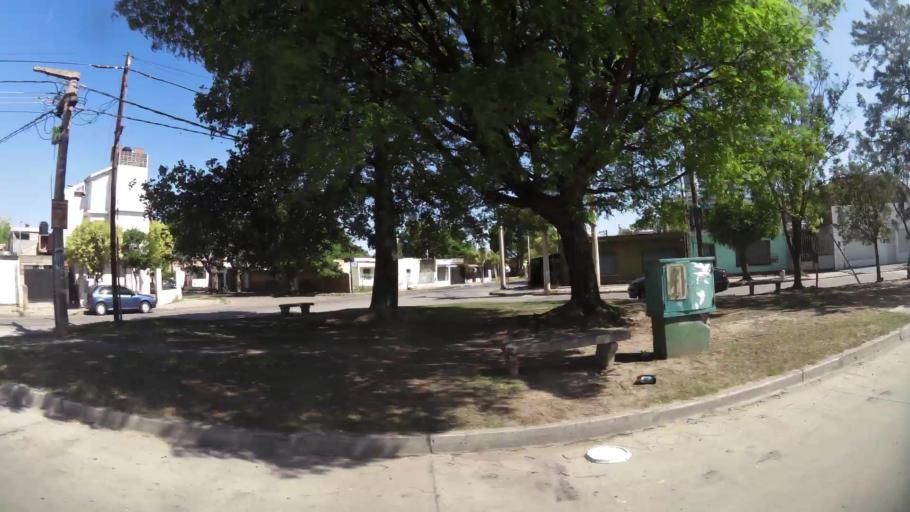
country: AR
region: Cordoba
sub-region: Departamento de Capital
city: Cordoba
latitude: -31.3656
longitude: -64.1498
